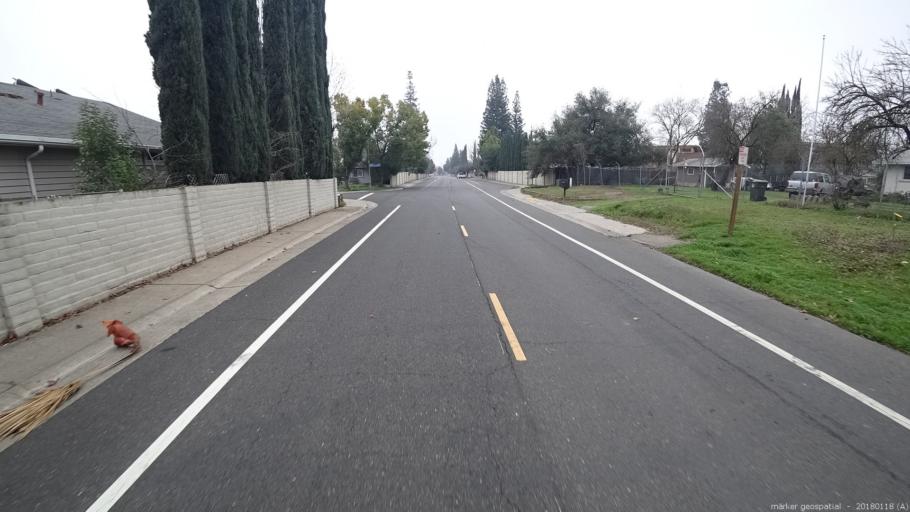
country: US
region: California
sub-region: Sacramento County
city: Rancho Cordova
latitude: 38.5838
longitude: -121.3230
